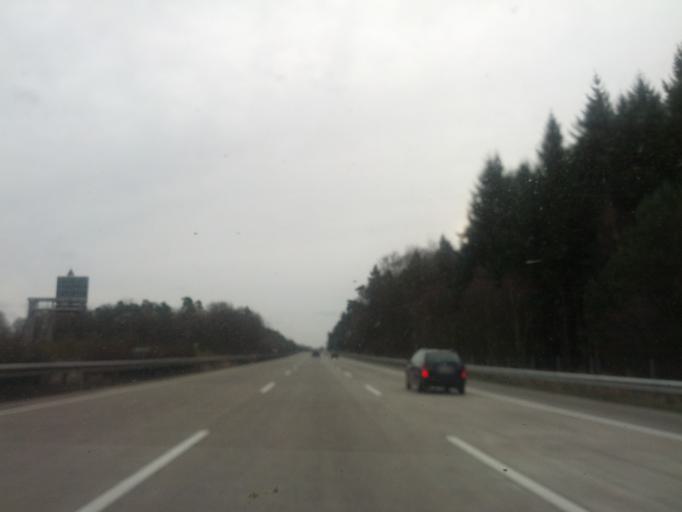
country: DE
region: Lower Saxony
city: Brackel
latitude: 53.3213
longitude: 10.0573
